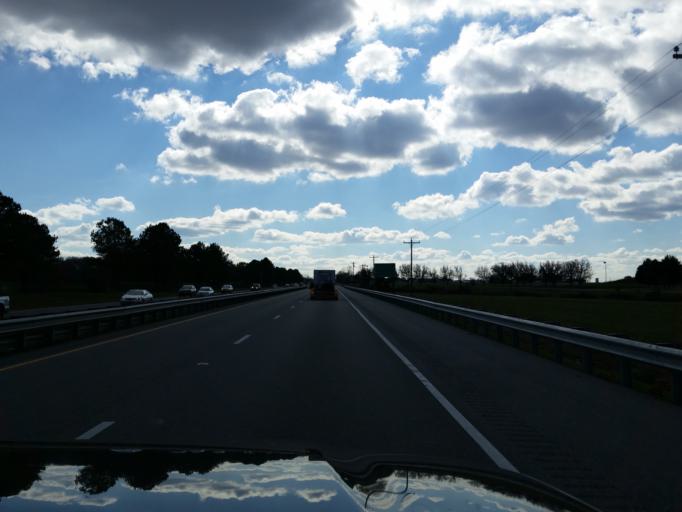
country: US
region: Maryland
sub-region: Talbot County
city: Easton
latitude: 38.8279
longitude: -76.0604
